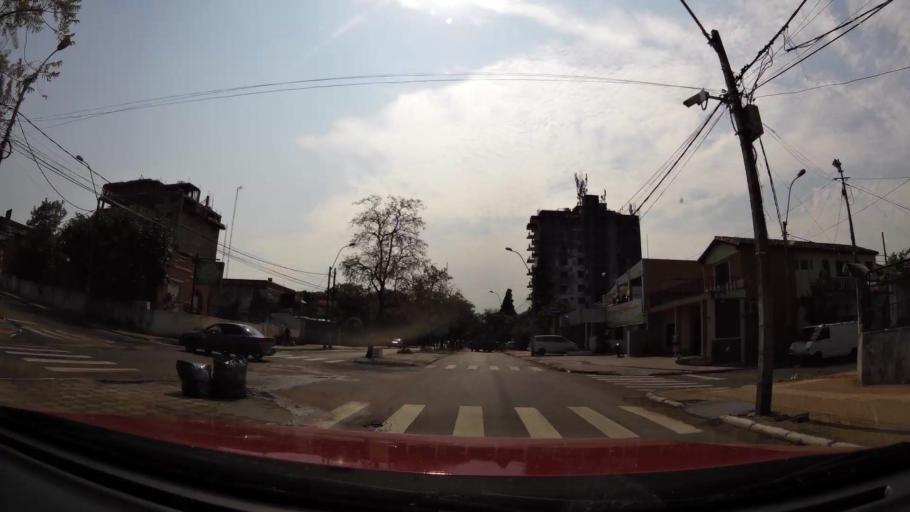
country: PY
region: Presidente Hayes
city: Nanawa
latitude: -25.2899
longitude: -57.6611
